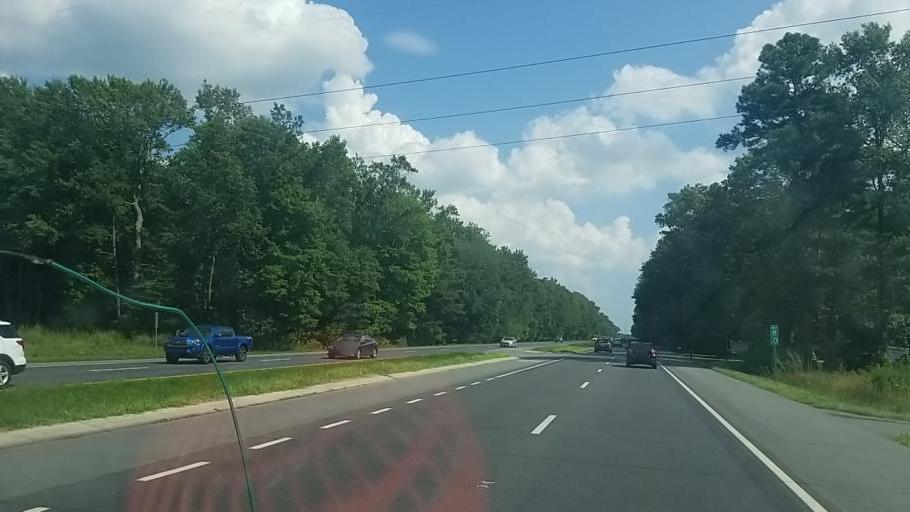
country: US
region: Delaware
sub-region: Sussex County
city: Millsboro
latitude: 38.5593
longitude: -75.2725
